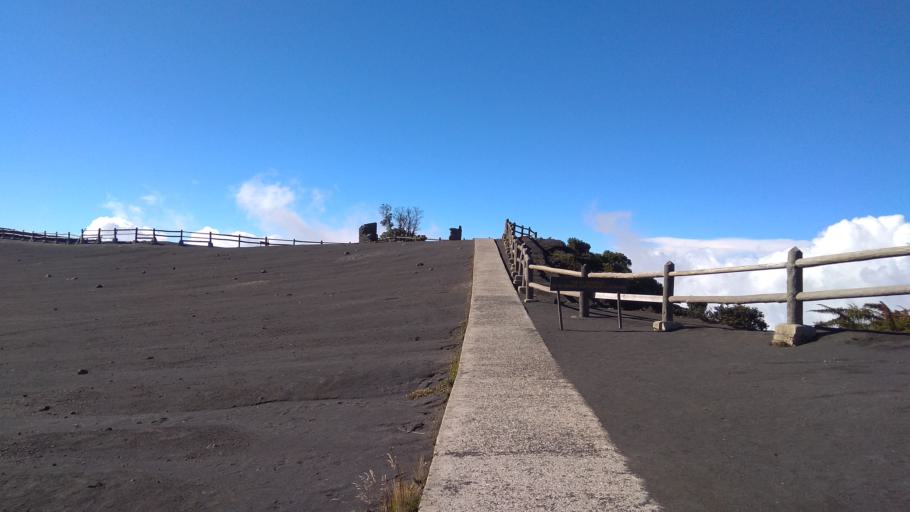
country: CR
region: Cartago
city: Cot
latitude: 9.9792
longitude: -83.8472
